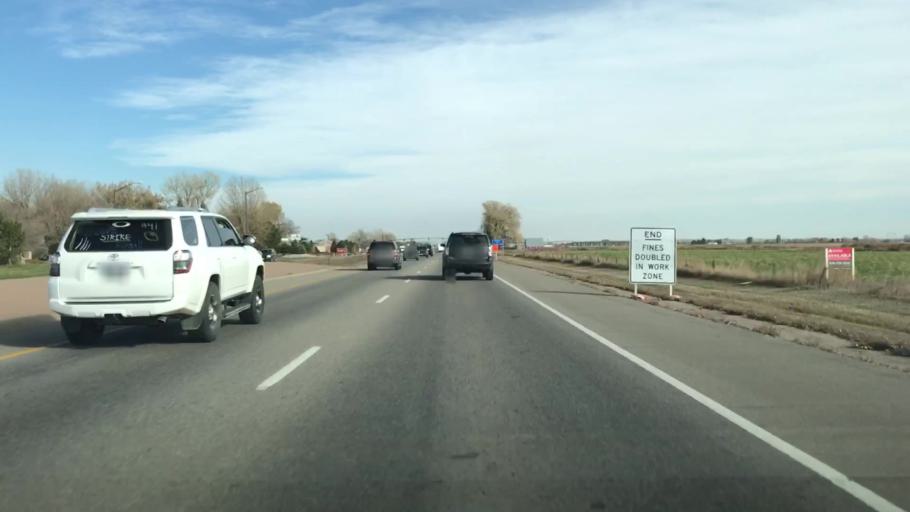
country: US
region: Colorado
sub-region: Larimer County
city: Loveland
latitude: 40.4071
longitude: -105.0167
